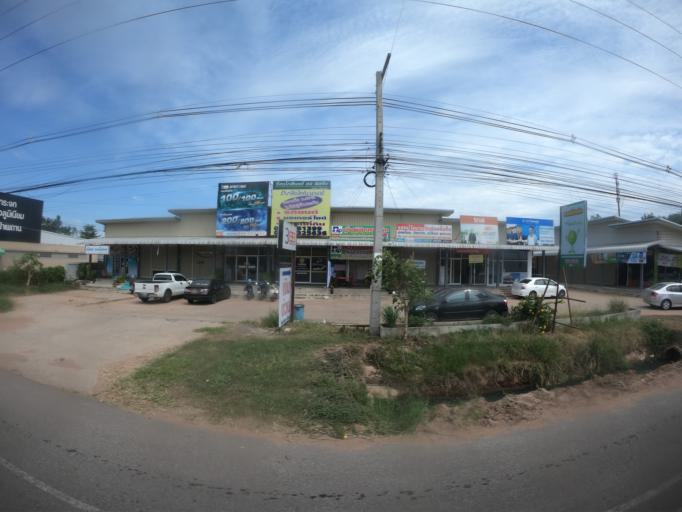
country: TH
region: Maha Sarakham
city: Chiang Yuen
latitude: 16.4123
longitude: 103.0920
